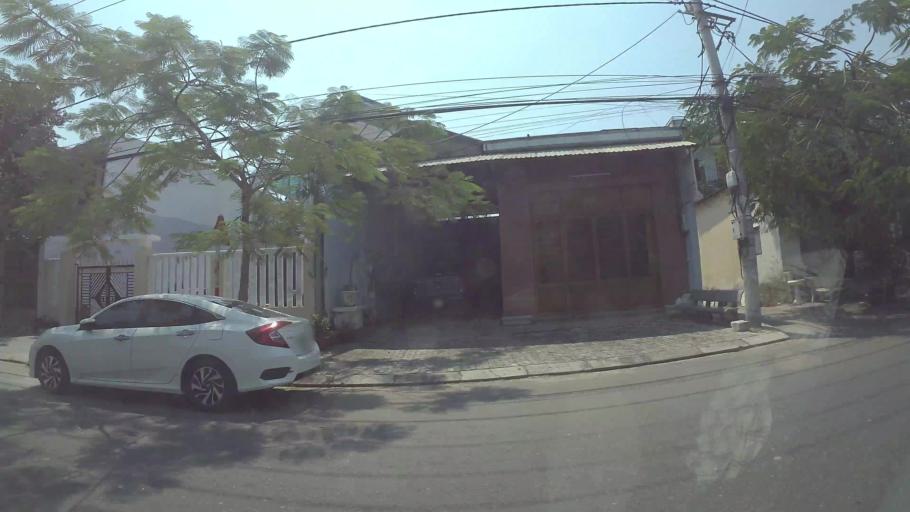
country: VN
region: Da Nang
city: Ngu Hanh Son
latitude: 15.9954
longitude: 108.2641
